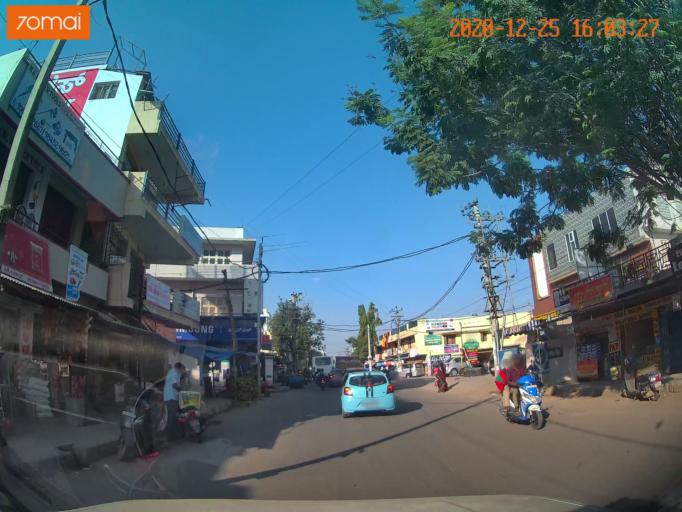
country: IN
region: Karnataka
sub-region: Bangalore Urban
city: Bangalore
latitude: 12.8848
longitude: 77.6250
